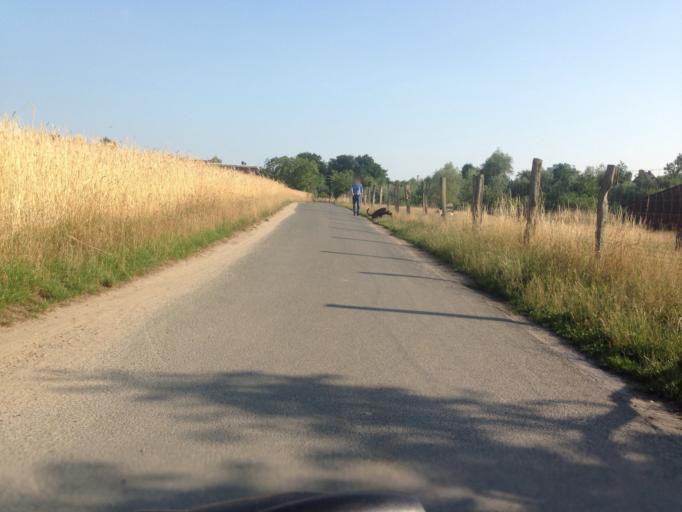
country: DE
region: North Rhine-Westphalia
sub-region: Regierungsbezirk Munster
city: Muenster
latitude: 51.9783
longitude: 7.6063
